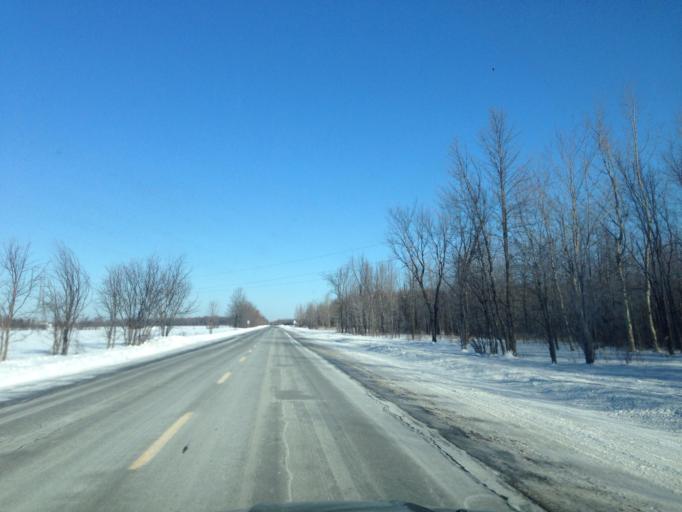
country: CA
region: Ontario
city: Clarence-Rockland
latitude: 45.3085
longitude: -75.4240
